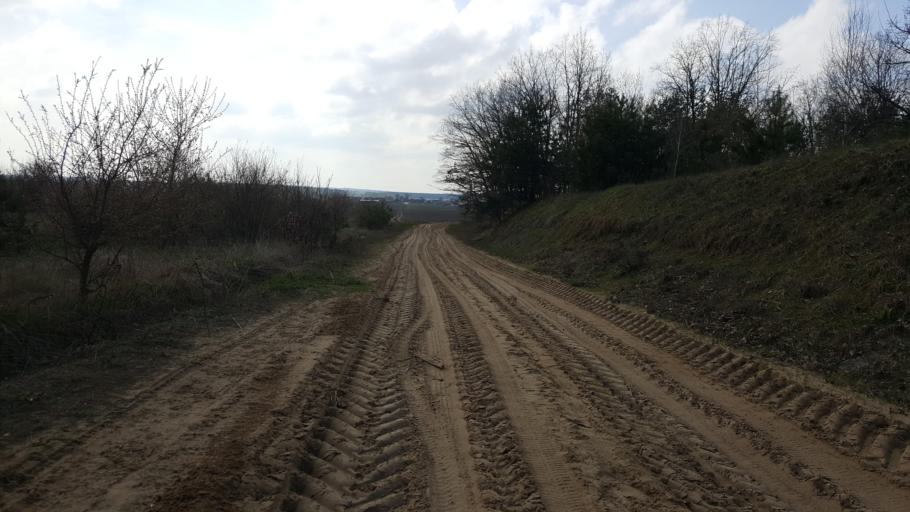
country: BY
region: Brest
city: Kamyanyets
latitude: 52.3288
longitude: 23.9333
